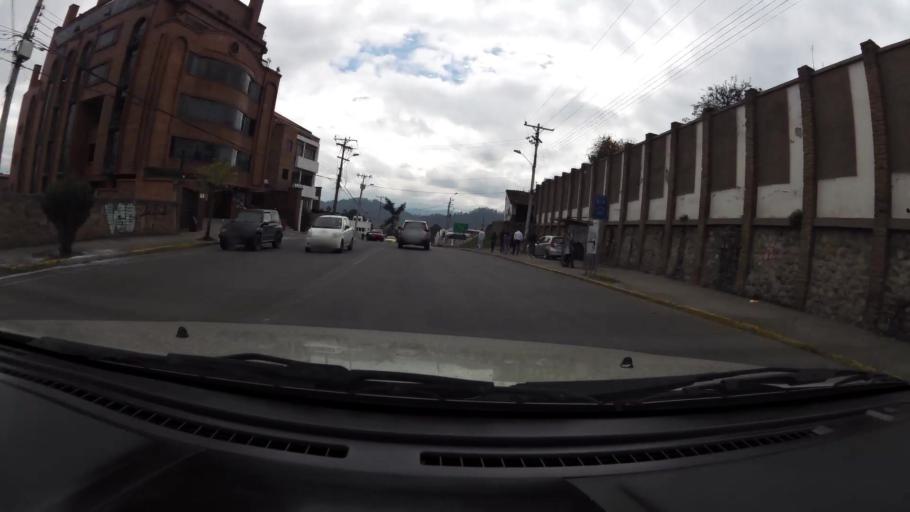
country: EC
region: Azuay
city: Cuenca
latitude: -2.9106
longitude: -79.0102
